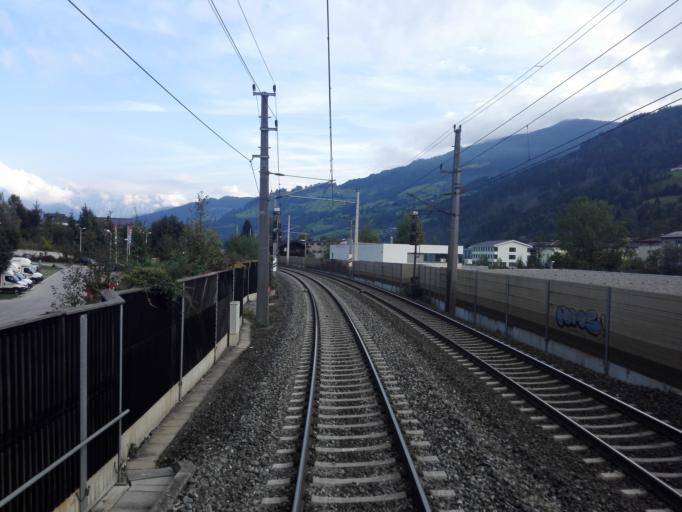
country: AT
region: Salzburg
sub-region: Politischer Bezirk Sankt Johann im Pongau
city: Sankt Johann im Pongau
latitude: 47.3564
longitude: 13.2009
